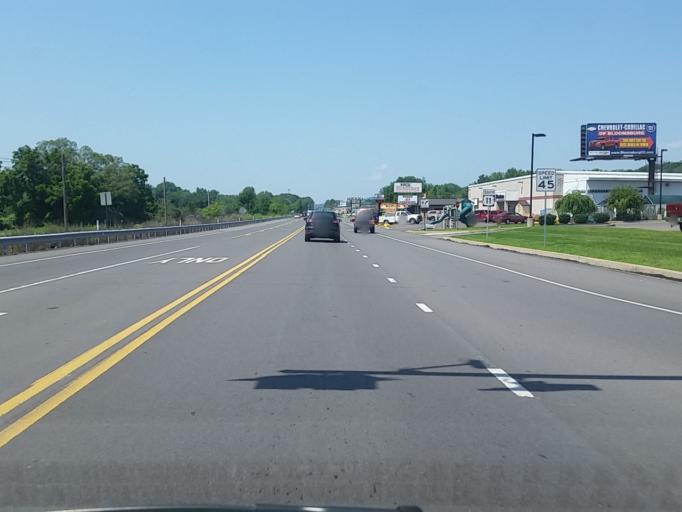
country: US
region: Pennsylvania
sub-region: Columbia County
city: Espy
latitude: 41.0111
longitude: -76.4143
